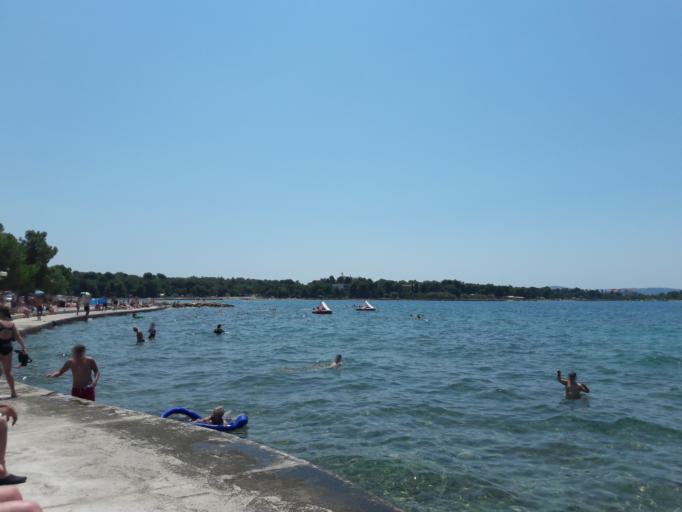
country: HR
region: Zadarska
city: Zadar
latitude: 44.1413
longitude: 15.2105
